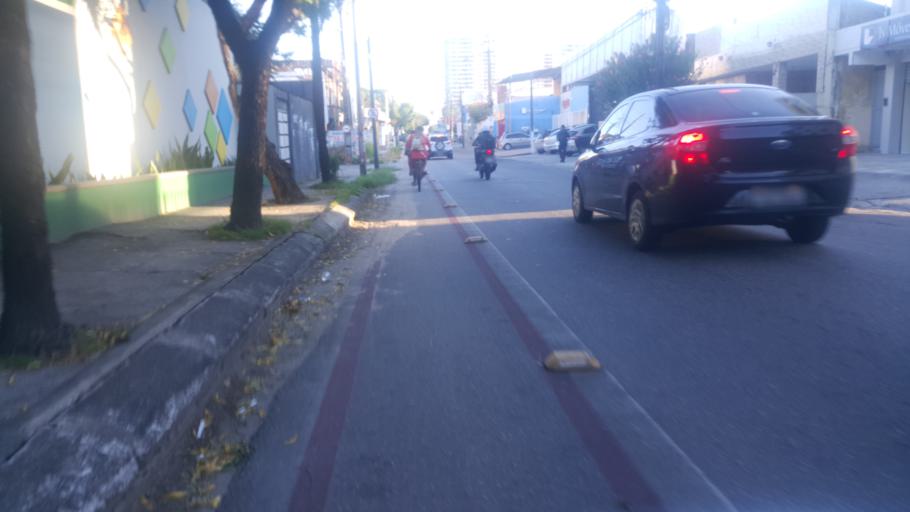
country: BR
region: Ceara
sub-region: Fortaleza
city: Fortaleza
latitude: -3.7432
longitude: -38.5345
